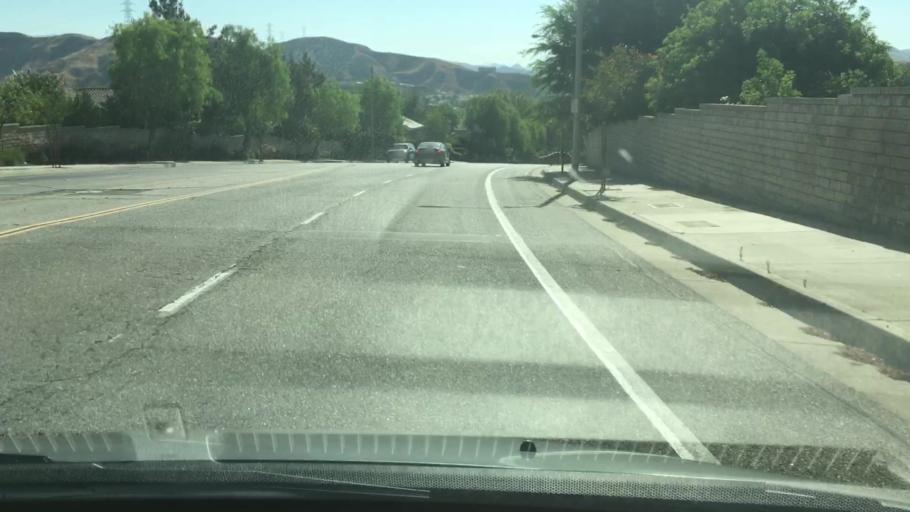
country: US
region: California
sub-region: Los Angeles County
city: Santa Clarita
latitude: 34.4596
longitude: -118.5180
